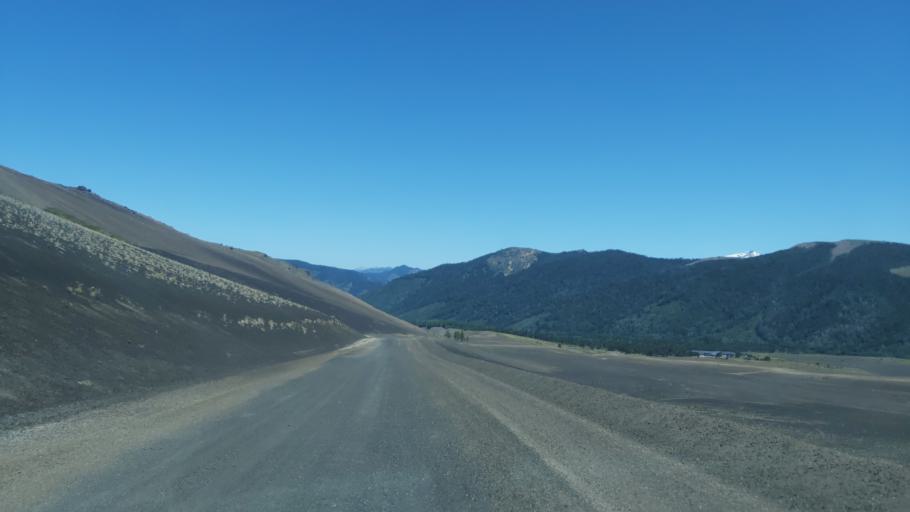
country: CL
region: Araucania
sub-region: Provincia de Cautin
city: Vilcun
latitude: -38.4041
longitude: -71.5438
